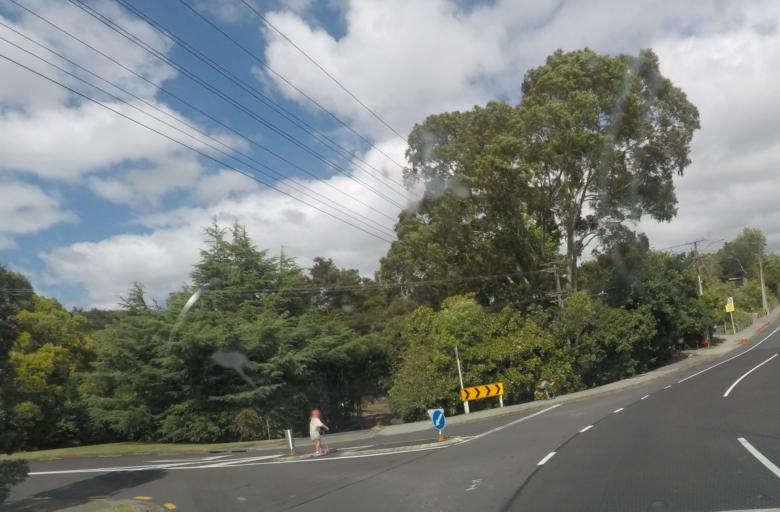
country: NZ
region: Auckland
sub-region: Auckland
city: North Shore
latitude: -36.7741
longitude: 174.6740
